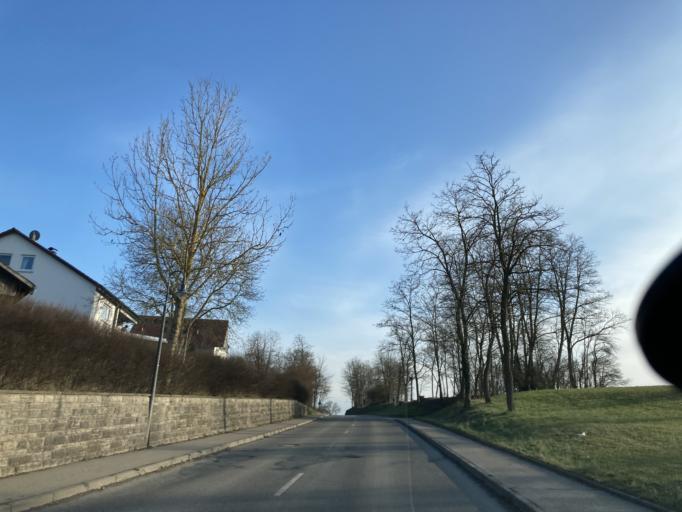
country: DE
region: Baden-Wuerttemberg
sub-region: Tuebingen Region
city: Hirrlingen
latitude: 48.4038
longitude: 8.8835
